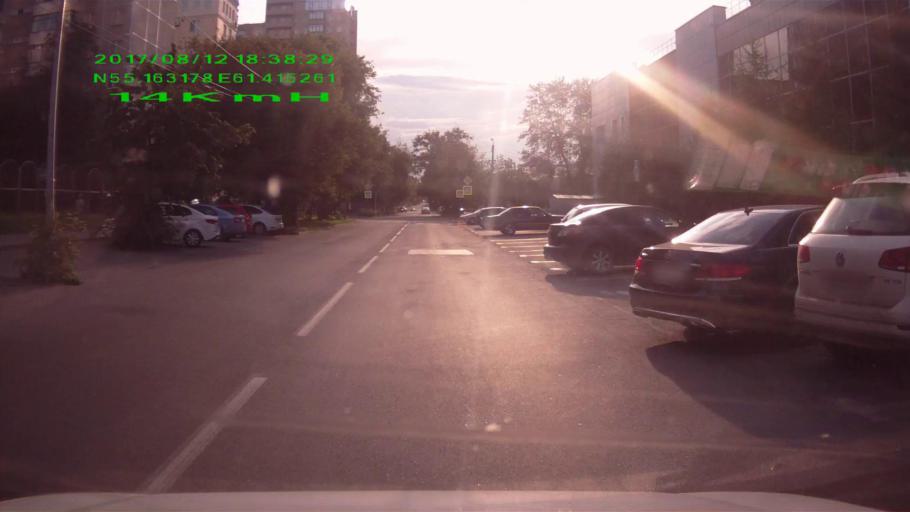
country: RU
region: Chelyabinsk
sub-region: Gorod Chelyabinsk
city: Chelyabinsk
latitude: 55.1617
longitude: 61.4084
